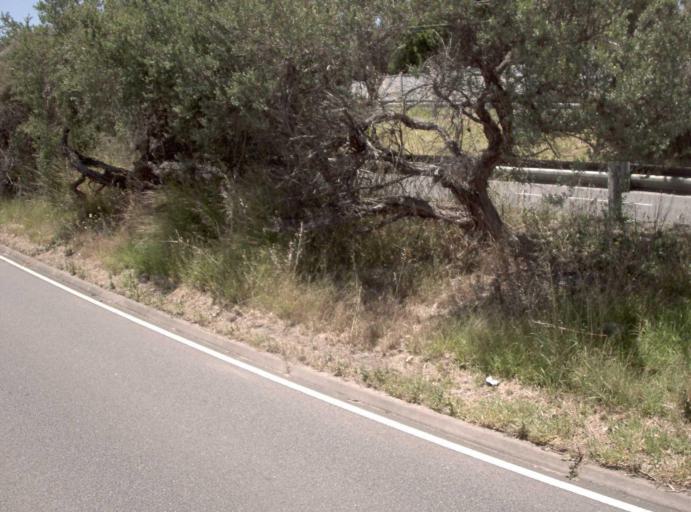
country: AU
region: Victoria
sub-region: Mornington Peninsula
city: Mount Eliza
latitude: -38.1650
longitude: 145.1016
